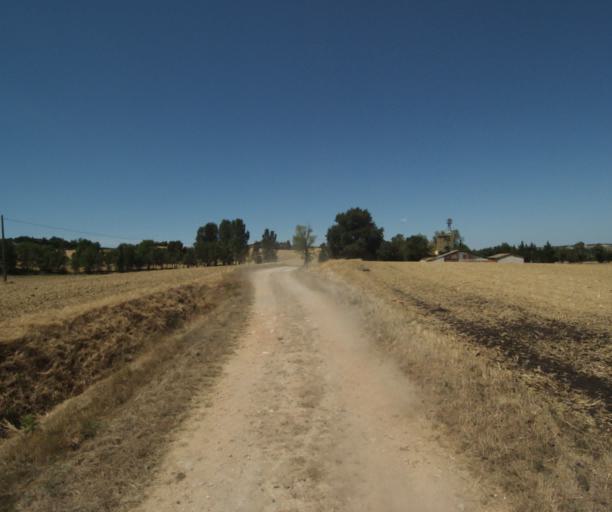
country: FR
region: Midi-Pyrenees
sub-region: Departement de la Haute-Garonne
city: Saint-Felix-Lauragais
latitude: 43.4540
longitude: 1.8985
